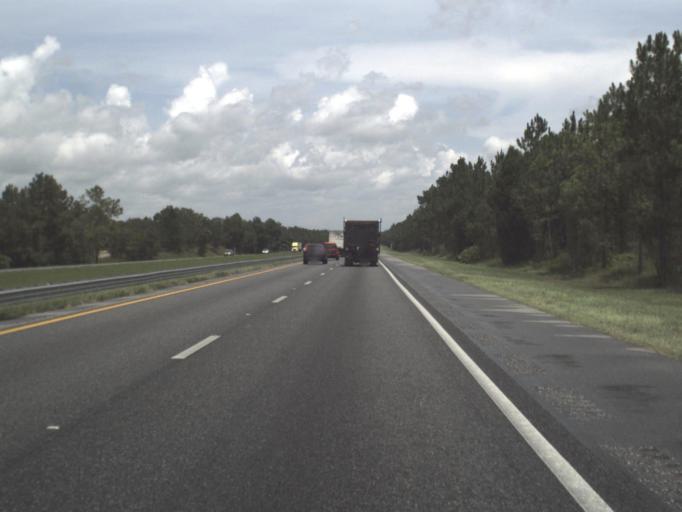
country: US
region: Florida
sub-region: Hernando County
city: Hill 'n Dale
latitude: 28.5422
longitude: -82.2369
